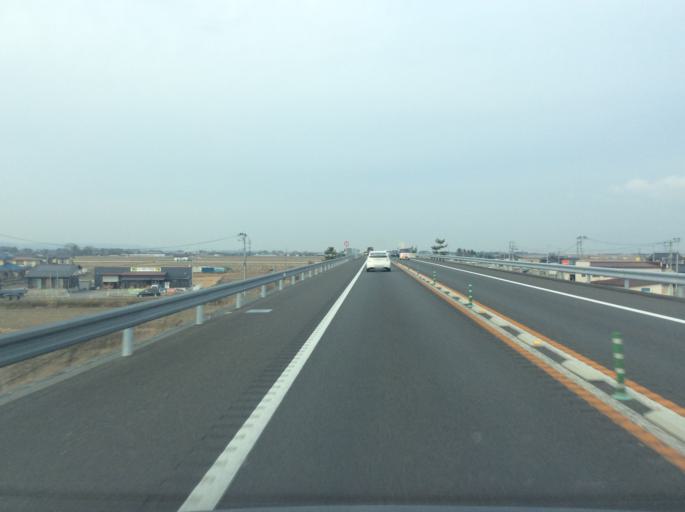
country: JP
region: Miyagi
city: Watari
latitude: 38.0429
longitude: 140.8931
